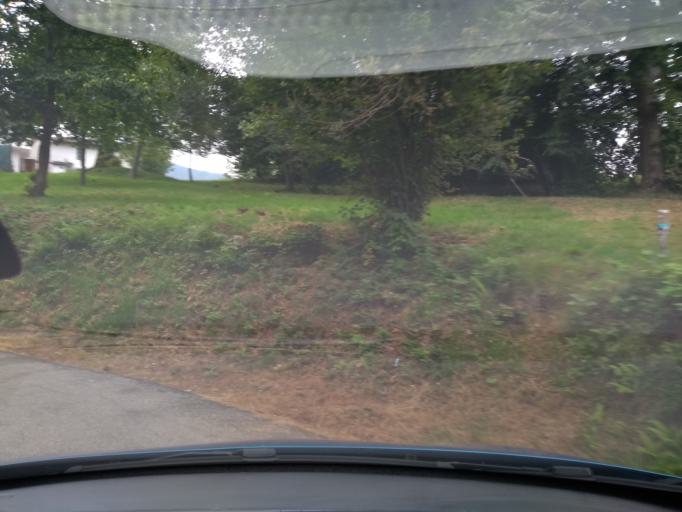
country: IT
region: Piedmont
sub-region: Provincia di Torino
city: La Villa
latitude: 45.2348
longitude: 7.4200
